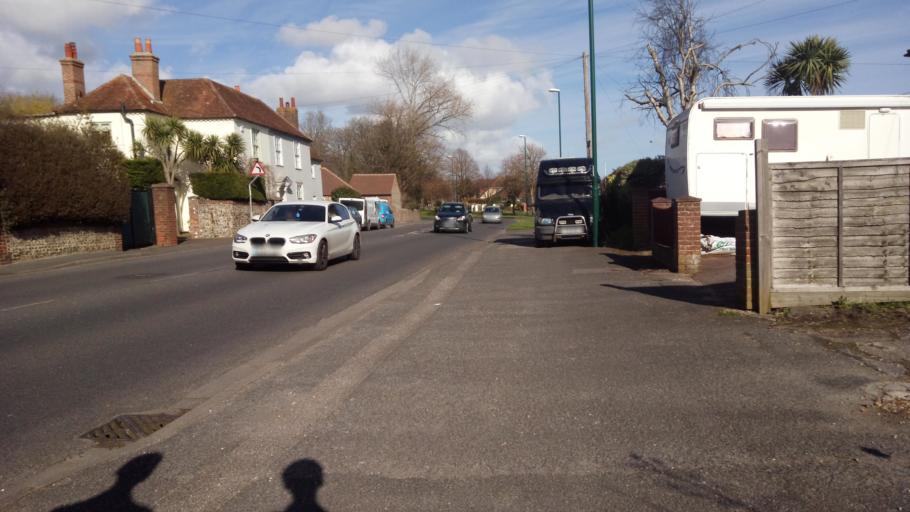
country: GB
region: England
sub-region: West Sussex
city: Bognor Regis
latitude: 50.7924
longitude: -0.6475
